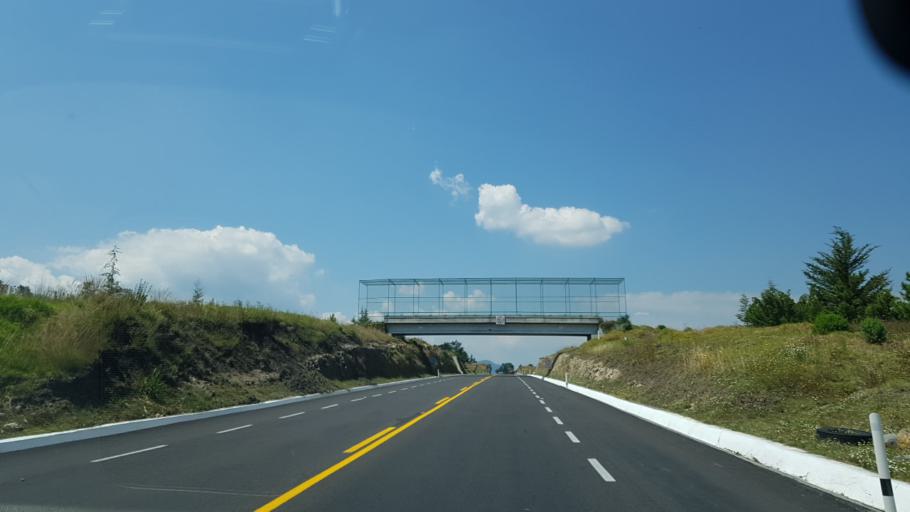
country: MX
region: Mexico
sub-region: Almoloya de Juarez
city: San Pedro de la Hortaliza (Ejido Almoloyan)
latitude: 19.3766
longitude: -99.8741
